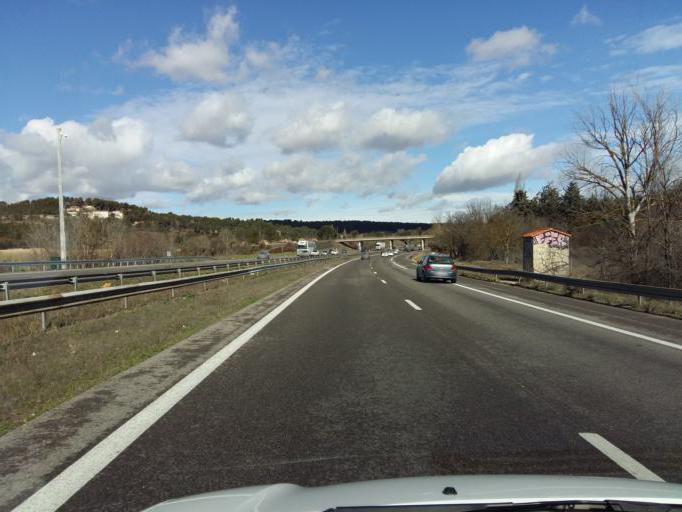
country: FR
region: Provence-Alpes-Cote d'Azur
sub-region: Departement des Bouches-du-Rhone
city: Bouc-Bel-Air
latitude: 43.4513
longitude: 5.3963
